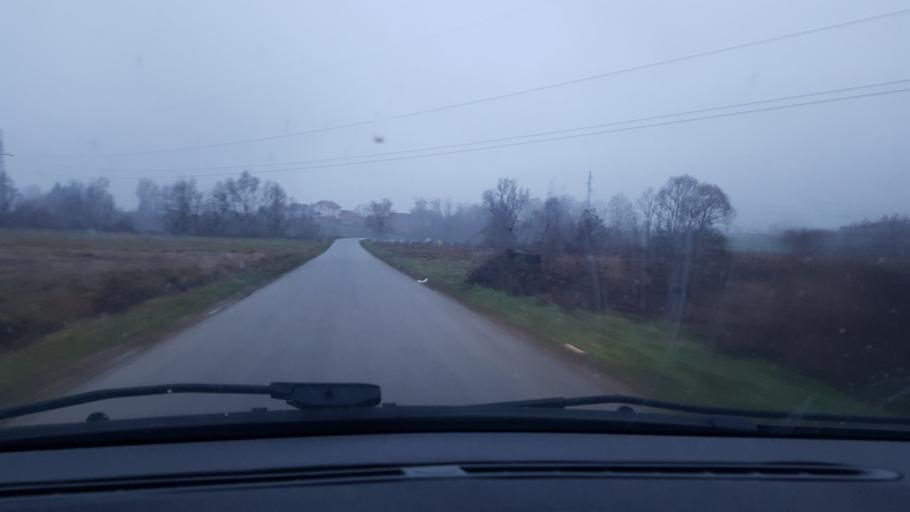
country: HR
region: Krapinsko-Zagorska
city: Zabok
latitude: 46.0396
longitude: 15.9216
